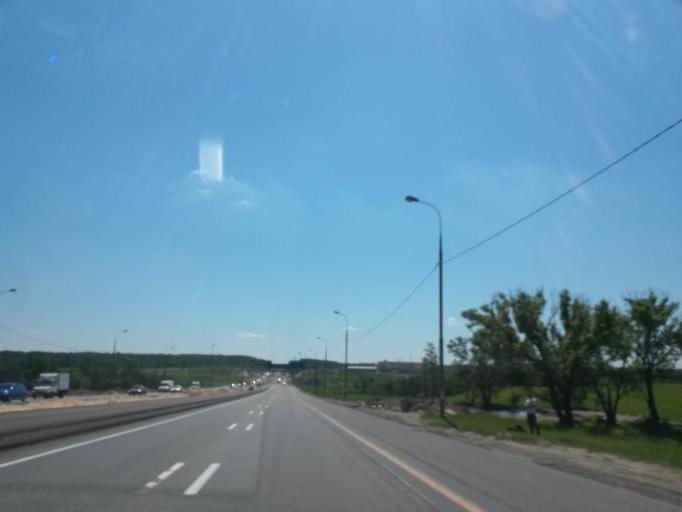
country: RU
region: Moskovskaya
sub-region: Chekhovskiy Rayon
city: Chekhov
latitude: 55.1371
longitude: 37.5611
